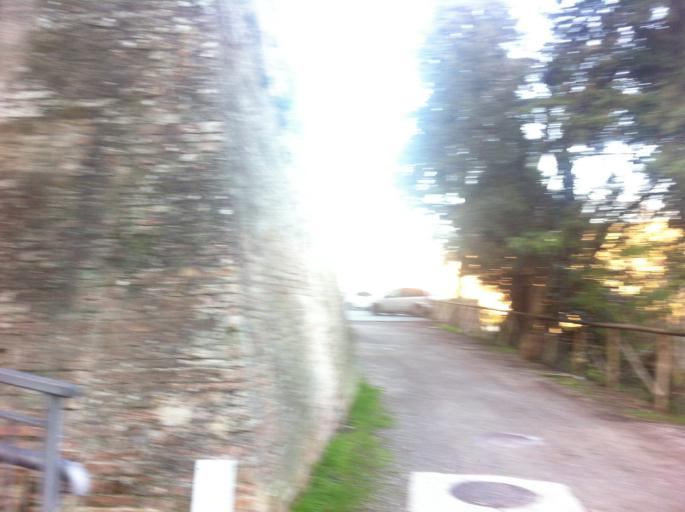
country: IT
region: Umbria
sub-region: Provincia di Perugia
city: Perugia
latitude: 43.1146
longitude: 12.3929
